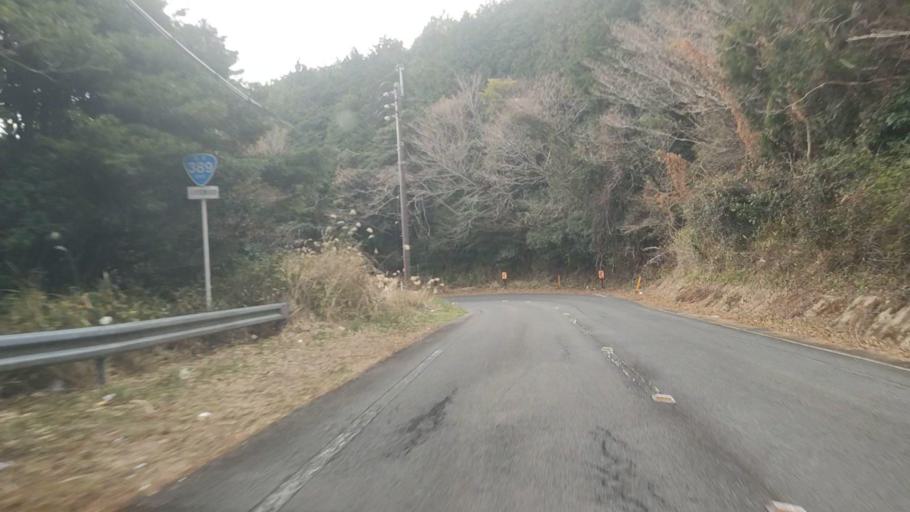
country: JP
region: Nagasaki
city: Shimabara
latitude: 32.7184
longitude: 130.2476
